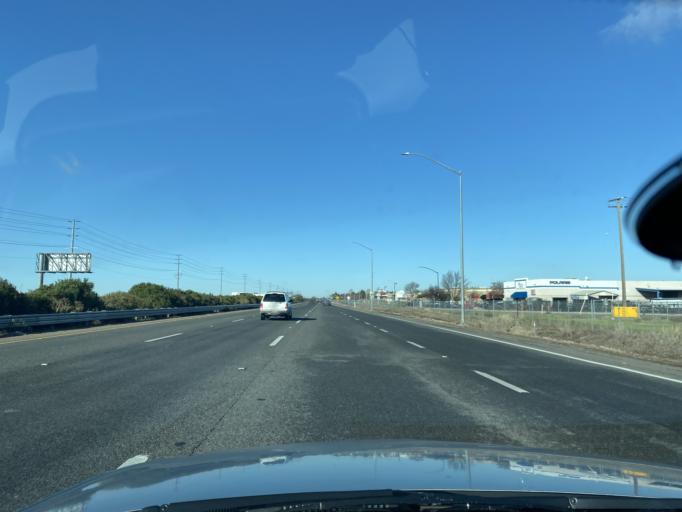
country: US
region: California
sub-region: Sacramento County
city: Elk Grove
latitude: 38.3796
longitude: -121.3650
